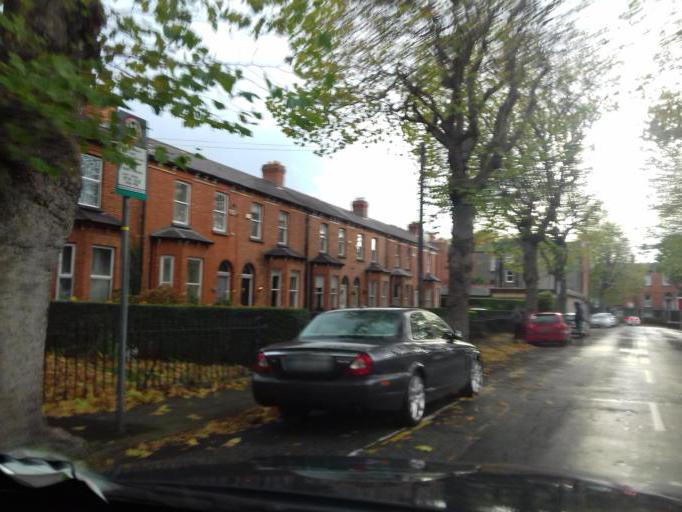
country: IE
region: Leinster
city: Cabra
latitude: 53.3598
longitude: -6.2825
